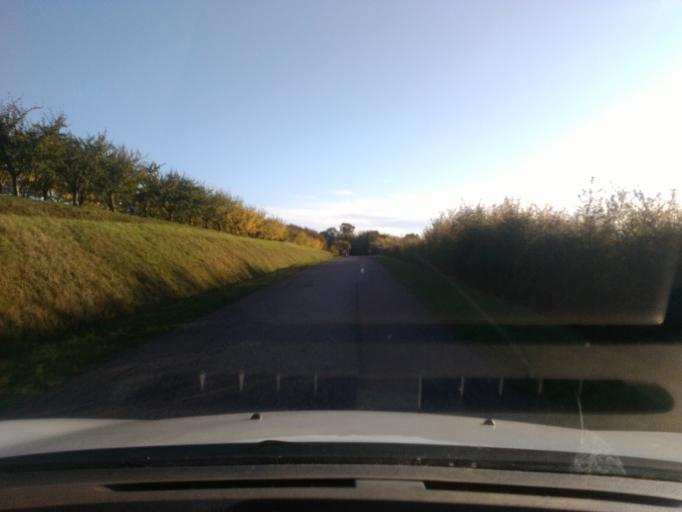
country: FR
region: Lorraine
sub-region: Departement des Vosges
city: Vincey
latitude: 48.3262
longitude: 6.3074
